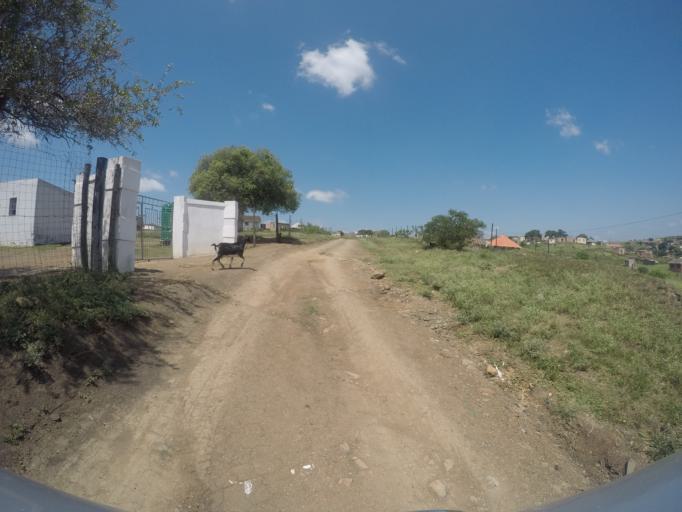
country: ZA
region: KwaZulu-Natal
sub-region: uThungulu District Municipality
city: Empangeni
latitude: -28.6072
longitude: 31.7375
